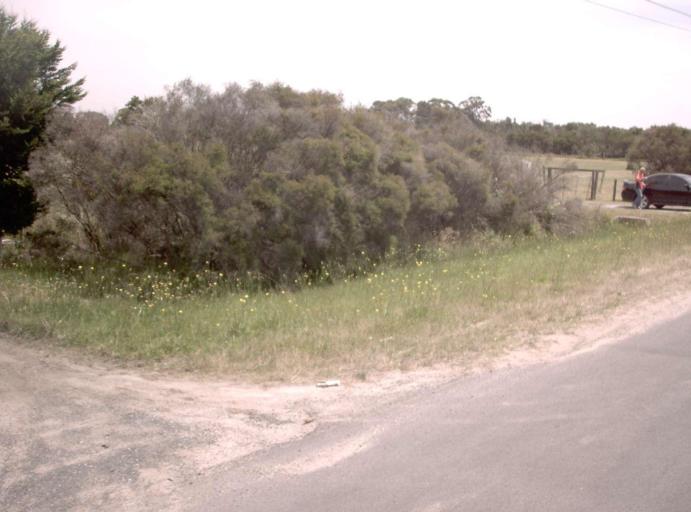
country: AU
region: Victoria
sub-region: Casey
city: Cranbourne South
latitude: -38.1185
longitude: 145.2311
